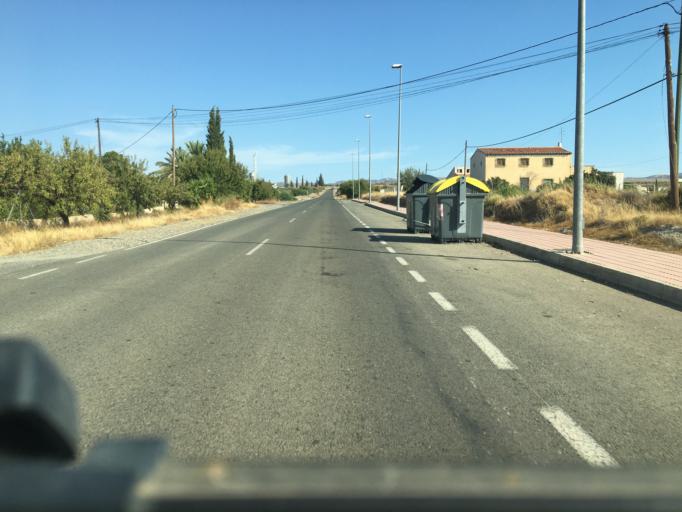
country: ES
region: Andalusia
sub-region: Provincia de Almeria
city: Huercal-Overa
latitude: 37.4492
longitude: -1.9850
